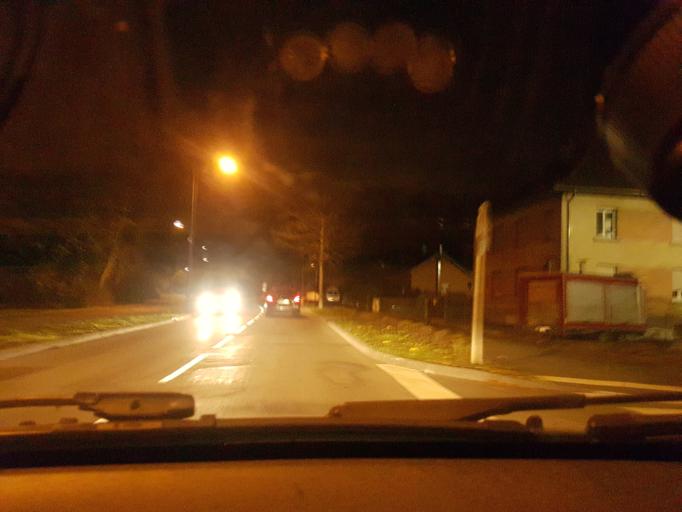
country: FR
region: Franche-Comte
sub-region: Territoire de Belfort
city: Danjoutin
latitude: 47.6232
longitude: 6.8631
